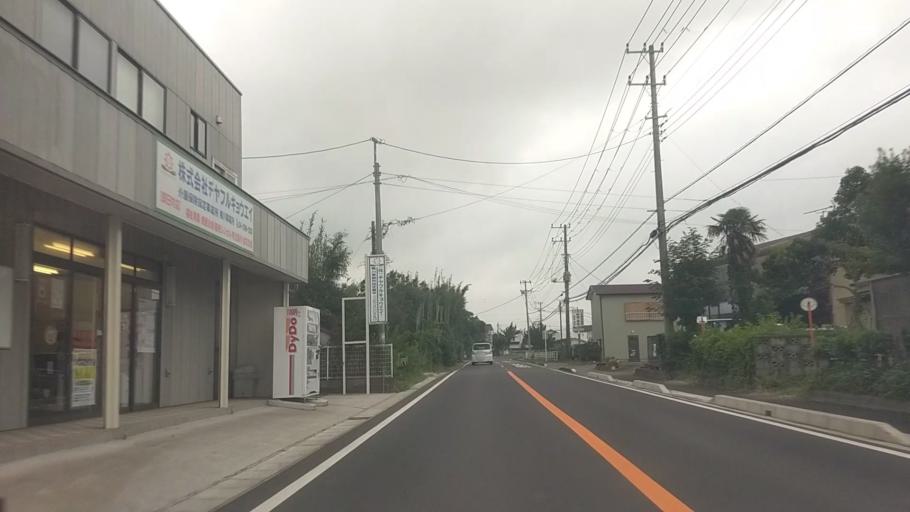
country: JP
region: Chiba
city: Kawaguchi
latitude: 35.1090
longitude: 140.0852
